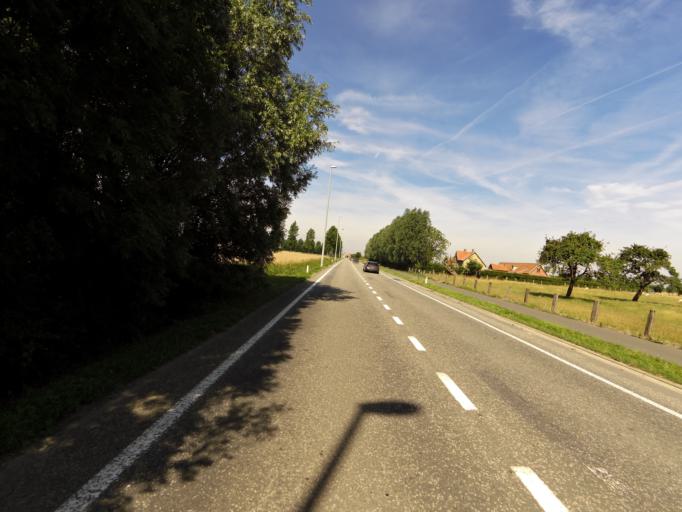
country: BE
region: Flanders
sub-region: Provincie West-Vlaanderen
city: Zuienkerke
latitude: 51.2369
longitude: 3.1716
